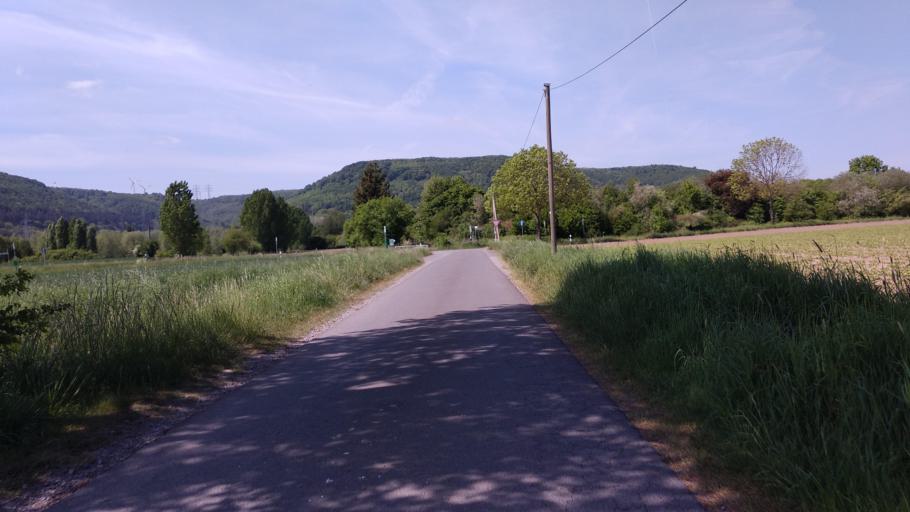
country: DE
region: North Rhine-Westphalia
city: Beverungen
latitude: 51.6468
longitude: 9.3942
